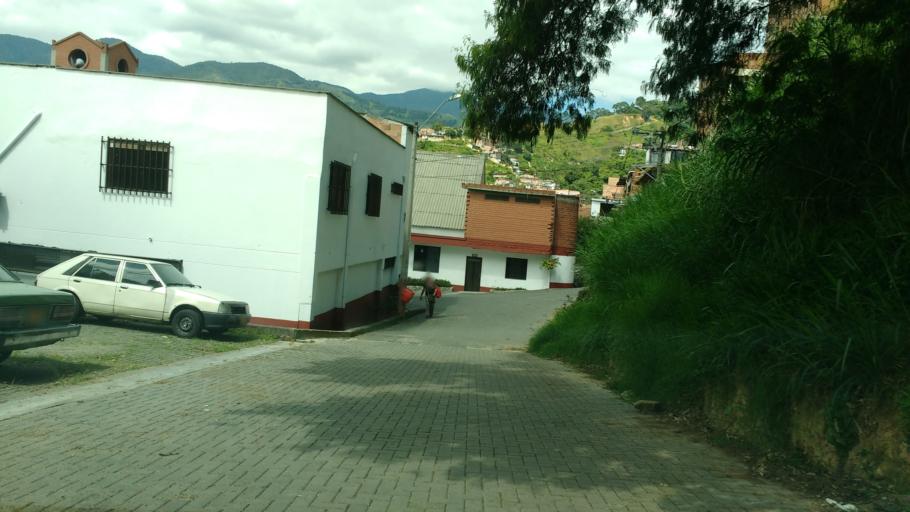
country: CO
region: Antioquia
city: Medellin
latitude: 6.2614
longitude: -75.6112
